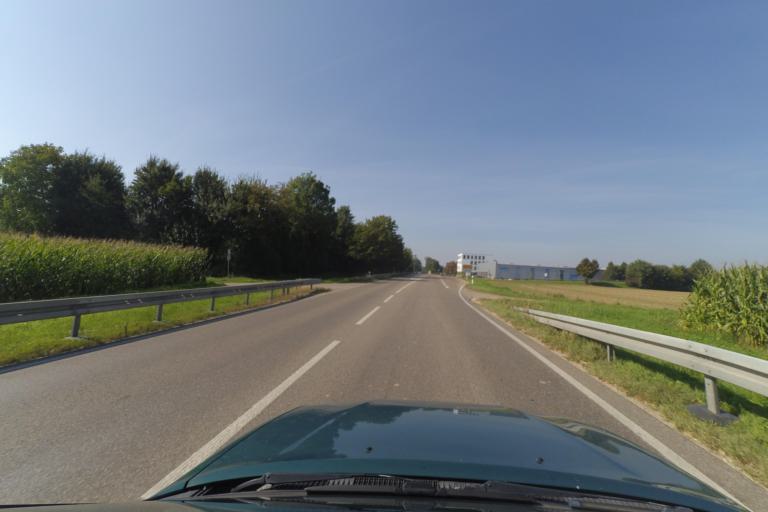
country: DE
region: Bavaria
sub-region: Swabia
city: Hochstadt an der Donau
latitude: 48.6240
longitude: 10.5784
